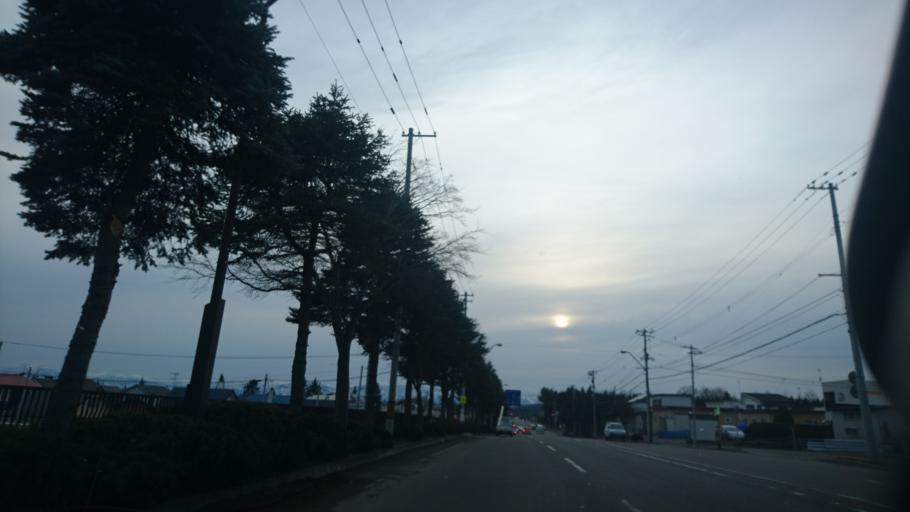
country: JP
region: Hokkaido
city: Otofuke
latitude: 42.9561
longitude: 143.1895
